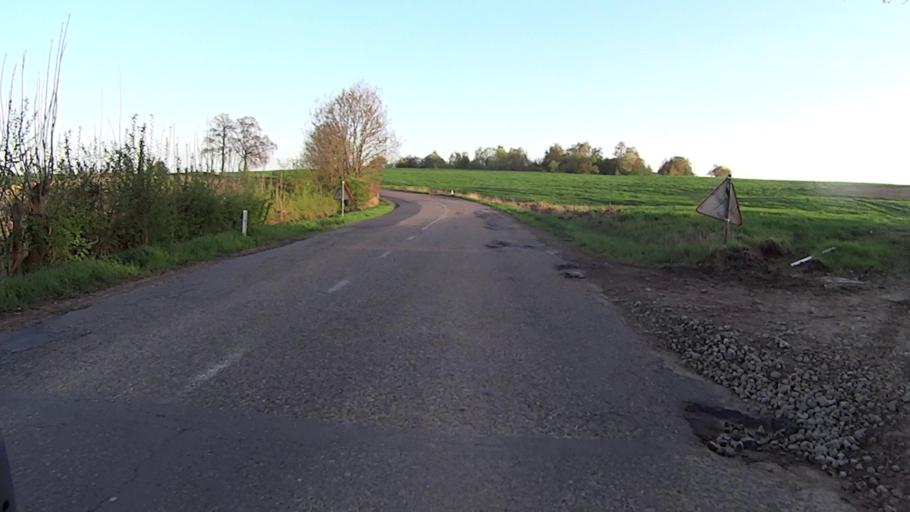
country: BE
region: Flanders
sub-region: Provincie Limburg
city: Sint-Pieters-Voeren
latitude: 50.7251
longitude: 5.7909
